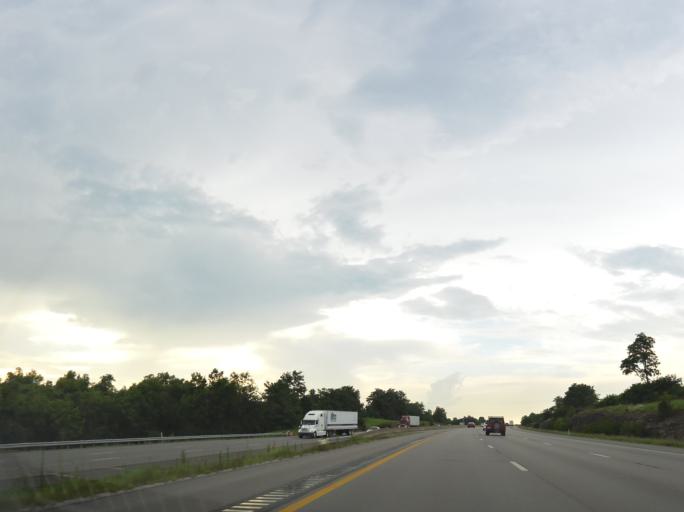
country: US
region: Kentucky
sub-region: Fayette County
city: Lexington
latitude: 37.9136
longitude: -84.3642
